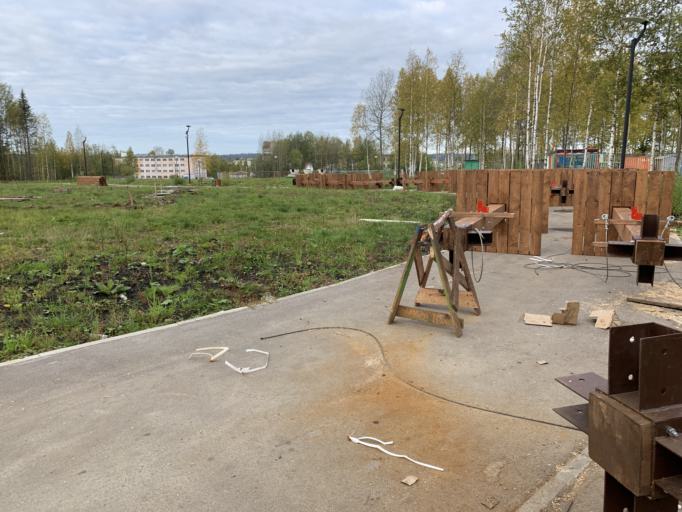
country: RU
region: Perm
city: Gubakha
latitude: 58.8327
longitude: 57.5643
